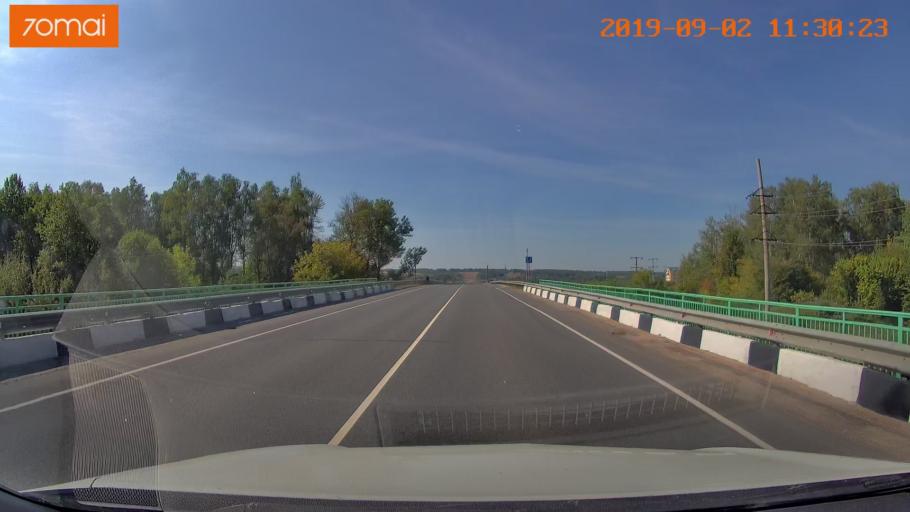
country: RU
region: Smolensk
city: Roslavl'
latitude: 53.9846
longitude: 32.8352
